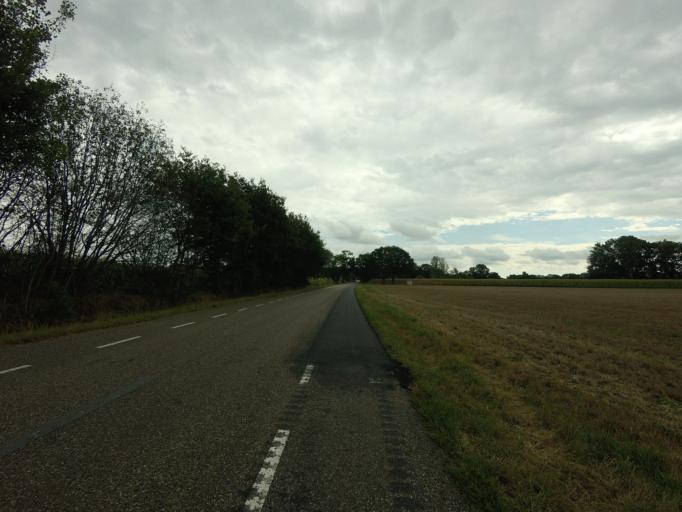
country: NL
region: Gelderland
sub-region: Gemeente Lochem
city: Laren
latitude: 52.2970
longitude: 6.3917
